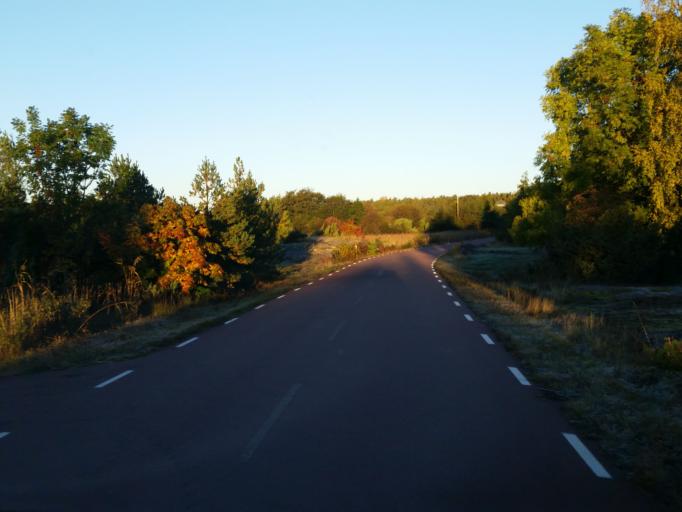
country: AX
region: Alands skaergard
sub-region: Vardoe
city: Vardoe
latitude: 60.3390
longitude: 20.3599
